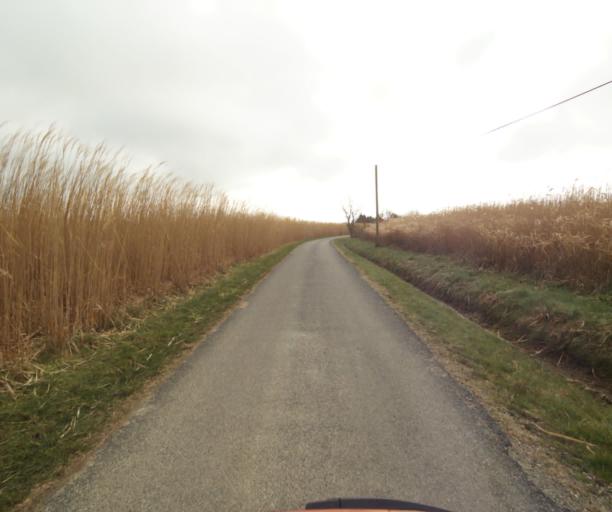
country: FR
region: Midi-Pyrenees
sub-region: Departement de l'Ariege
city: Mazeres
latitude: 43.1970
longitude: 1.6712
